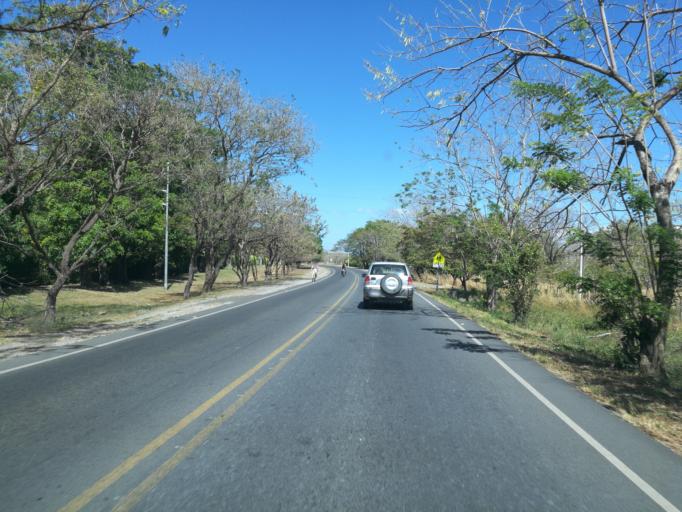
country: CR
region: Guanacaste
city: Liberia
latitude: 10.6441
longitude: -85.4552
